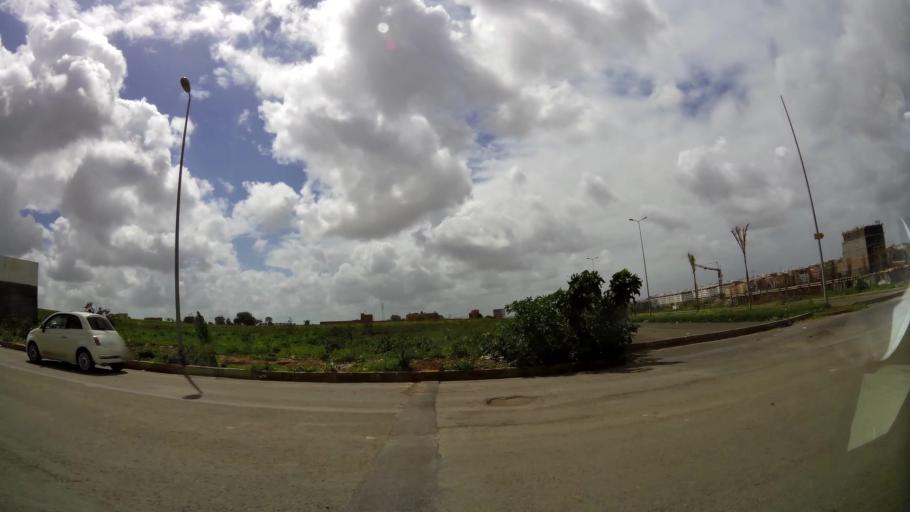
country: MA
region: Grand Casablanca
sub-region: Casablanca
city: Casablanca
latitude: 33.5265
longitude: -7.6021
